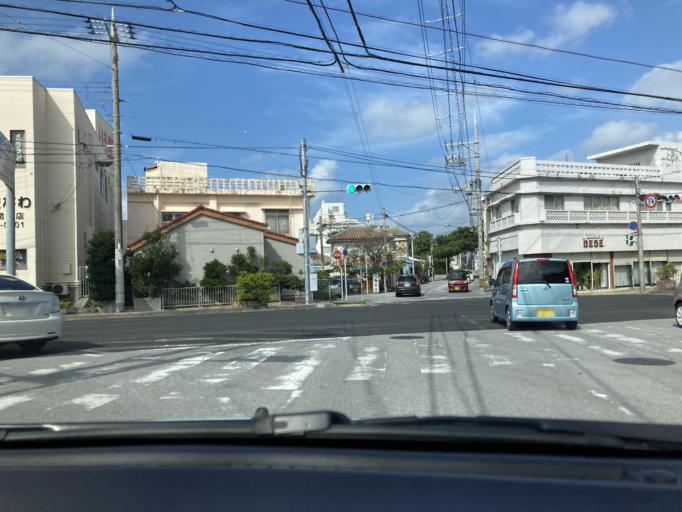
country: JP
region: Okinawa
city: Chatan
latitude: 26.2898
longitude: 127.7780
